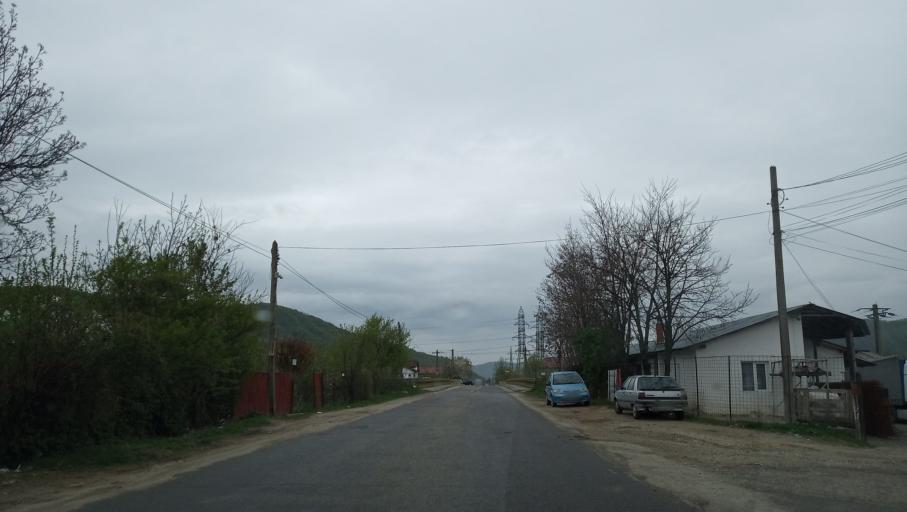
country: RO
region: Valcea
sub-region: Oras Calimanesti
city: Jiblea Veche
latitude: 45.2376
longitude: 24.3649
